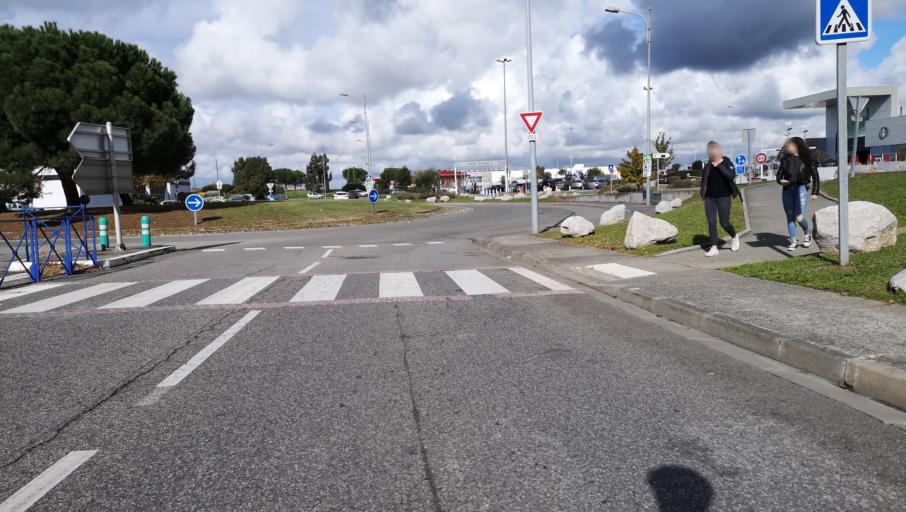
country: FR
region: Midi-Pyrenees
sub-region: Departement de la Haute-Garonne
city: Beauzelle
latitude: 43.6446
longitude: 1.3694
